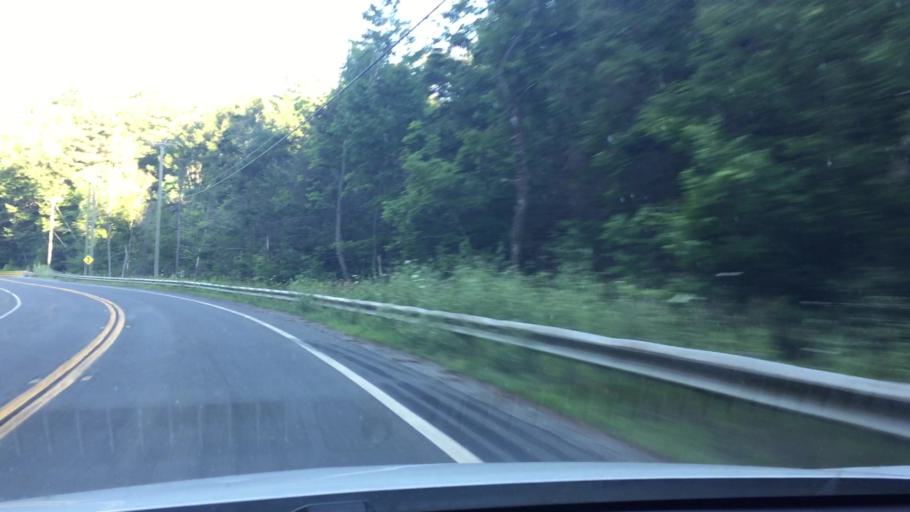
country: US
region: Massachusetts
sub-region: Berkshire County
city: Becket
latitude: 42.2703
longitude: -73.0195
